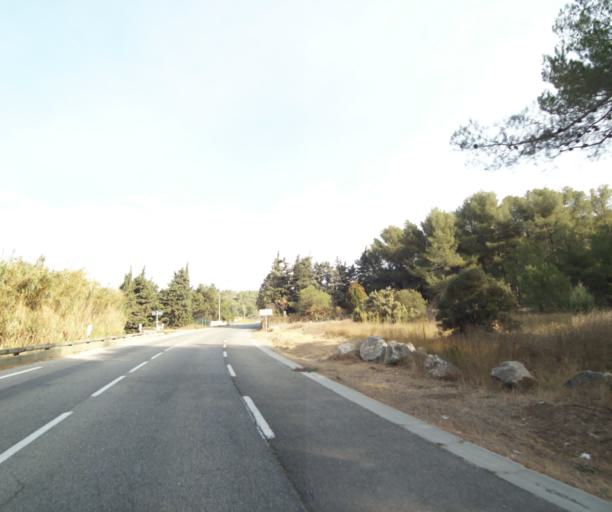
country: FR
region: Provence-Alpes-Cote d'Azur
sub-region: Departement des Bouches-du-Rhone
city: Ensues-la-Redonne
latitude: 43.3523
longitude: 5.1832
